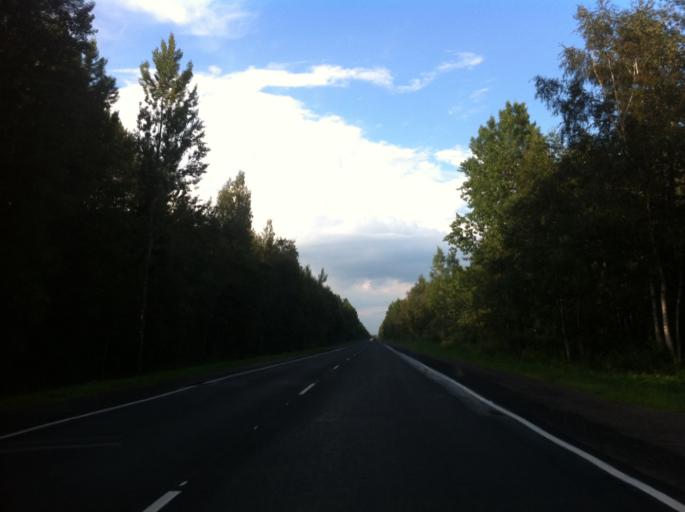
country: RU
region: Leningrad
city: Luga
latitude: 58.4872
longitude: 29.7794
